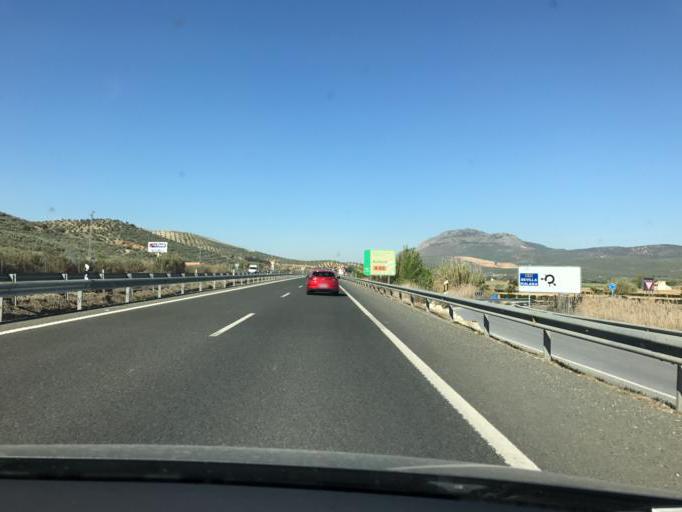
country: ES
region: Andalusia
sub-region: Provincia de Granada
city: Huetor-Tajar
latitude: 37.1808
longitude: -4.0557
